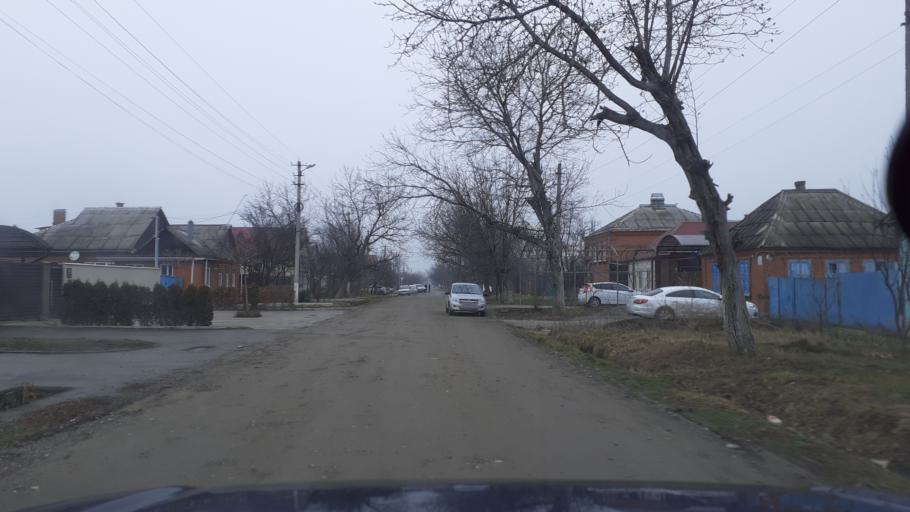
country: RU
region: Adygeya
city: Maykop
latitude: 44.6165
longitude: 40.0877
